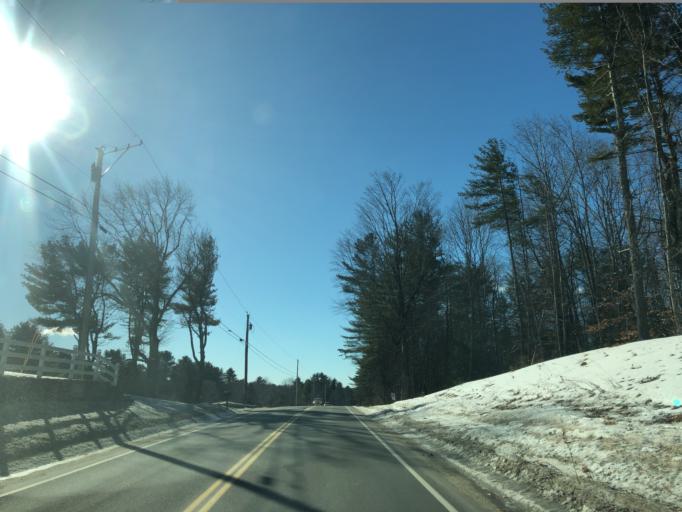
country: US
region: Maine
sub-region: Cumberland County
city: South Windham
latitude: 43.7717
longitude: -70.4393
